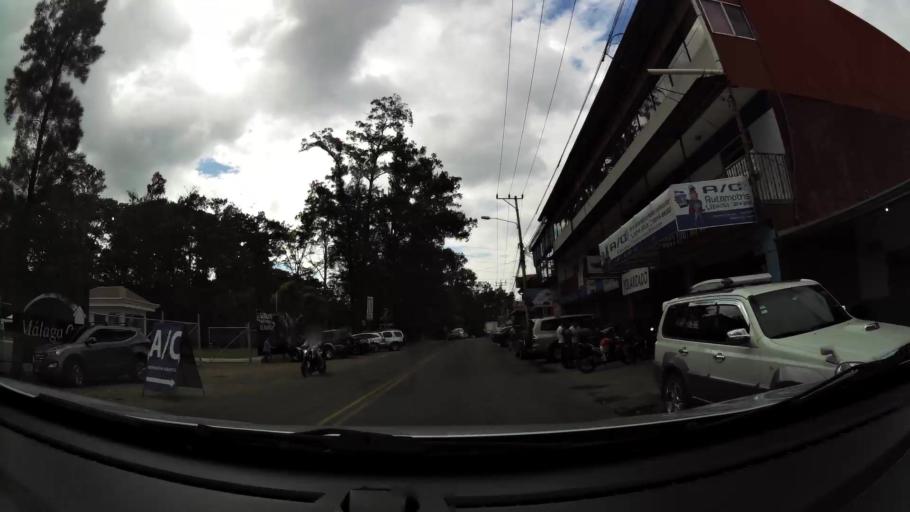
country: CR
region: San Jose
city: San Felipe
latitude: 9.9116
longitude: -84.1103
